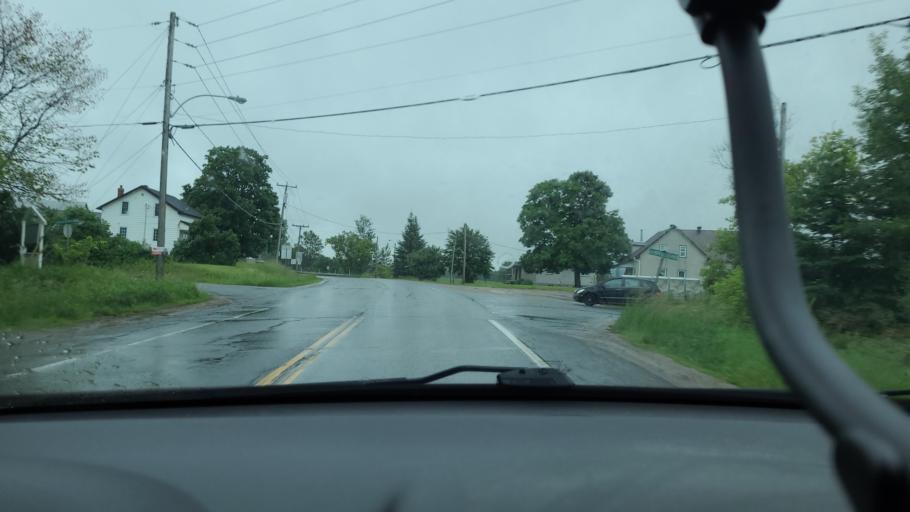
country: CA
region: Quebec
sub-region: Outaouais
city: Saint-Andre-Avellin
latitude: 45.7877
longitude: -75.0685
